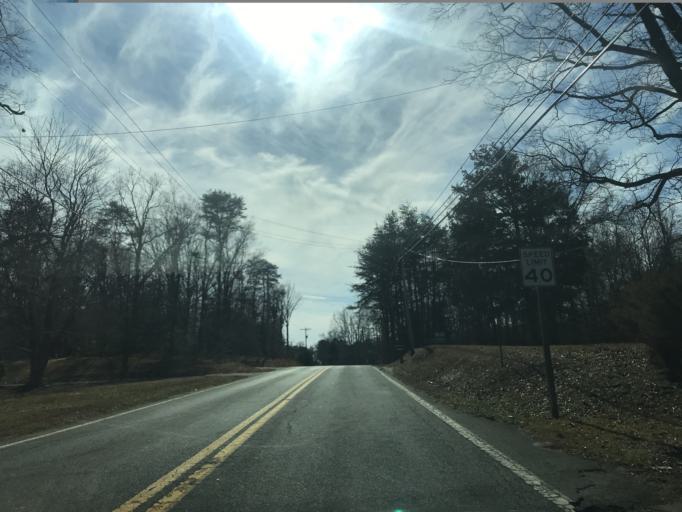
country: US
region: Maryland
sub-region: Charles County
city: Potomac Heights
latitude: 38.5628
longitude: -77.1287
